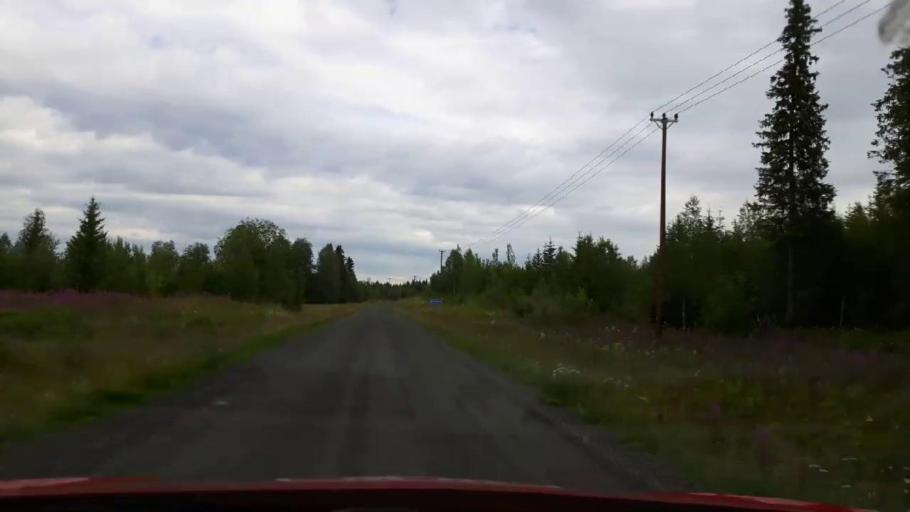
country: SE
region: Jaemtland
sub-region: Stroemsunds Kommun
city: Stroemsund
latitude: 63.4857
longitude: 15.3067
